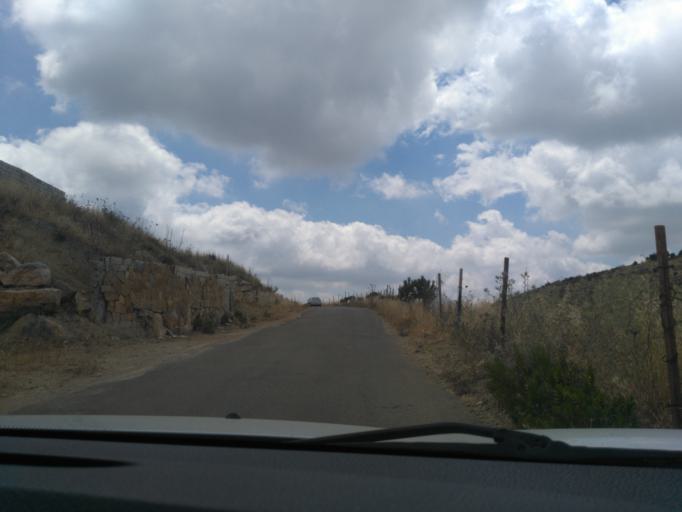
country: LB
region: Mont-Liban
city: Beit ed Dine
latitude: 33.6829
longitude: 35.6652
